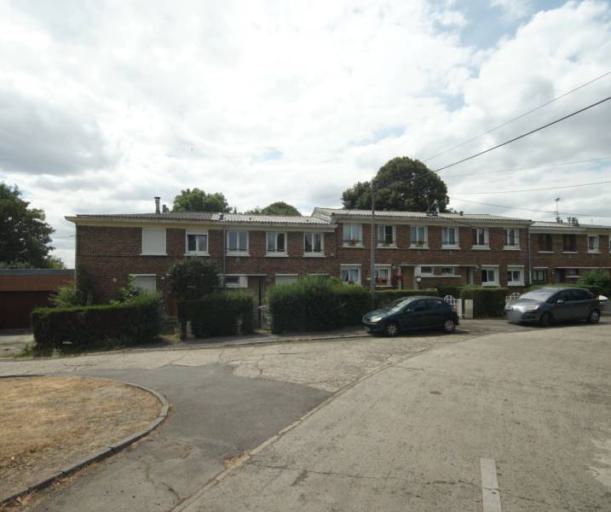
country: FR
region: Nord-Pas-de-Calais
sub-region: Departement du Nord
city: Mouvaux
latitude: 50.6975
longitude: 3.1441
